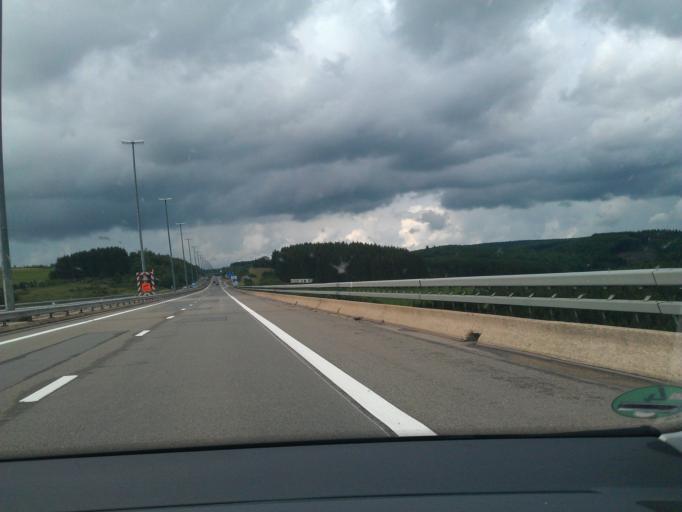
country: DE
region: Rheinland-Pfalz
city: Winterspelt
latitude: 50.2388
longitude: 6.1801
